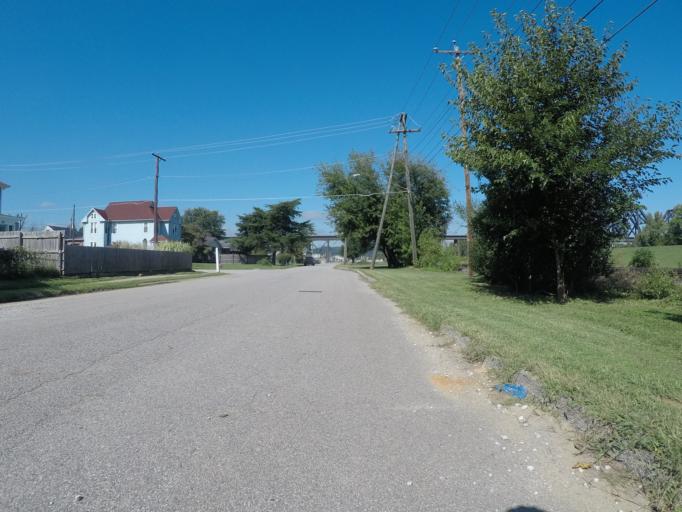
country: US
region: West Virginia
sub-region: Wayne County
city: Kenova
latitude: 38.4018
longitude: -82.5726
